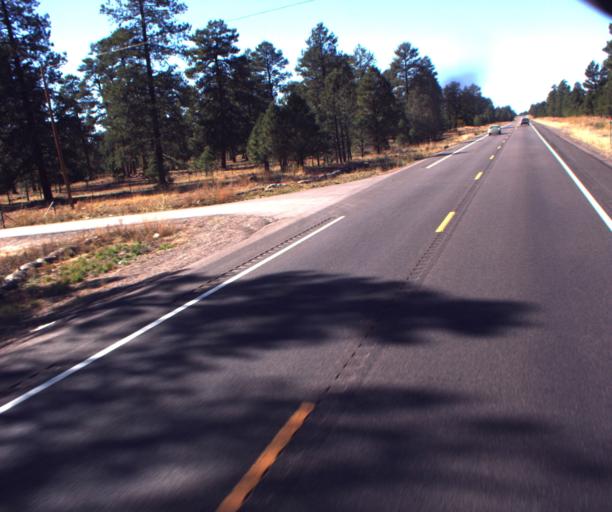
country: US
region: Arizona
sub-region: Apache County
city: Saint Michaels
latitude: 35.6895
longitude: -109.2521
